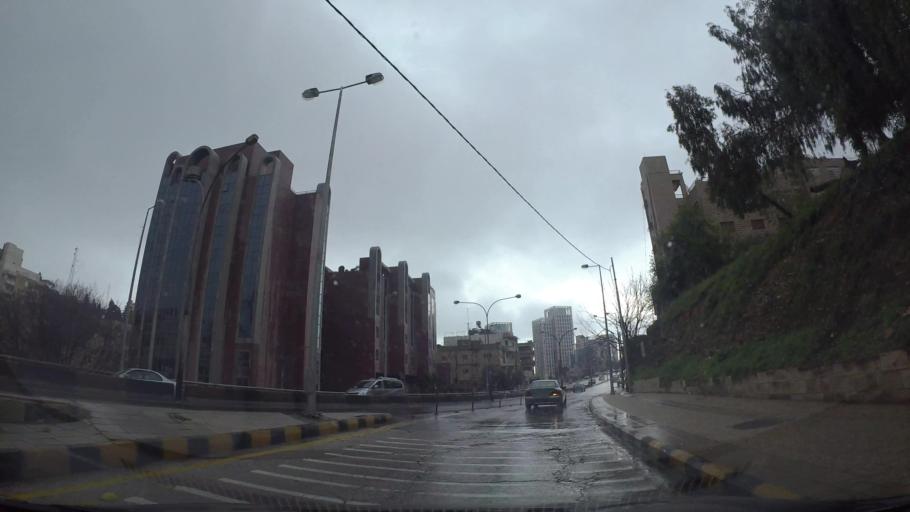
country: JO
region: Amman
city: Amman
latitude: 31.9590
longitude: 35.9060
